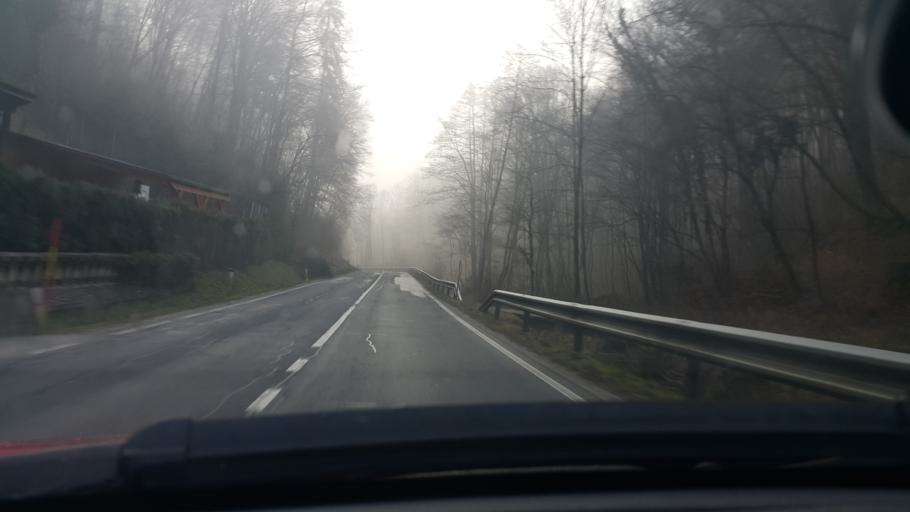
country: SI
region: Rogaska Slatina
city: Rogaska Slatina
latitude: 46.2160
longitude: 15.5826
